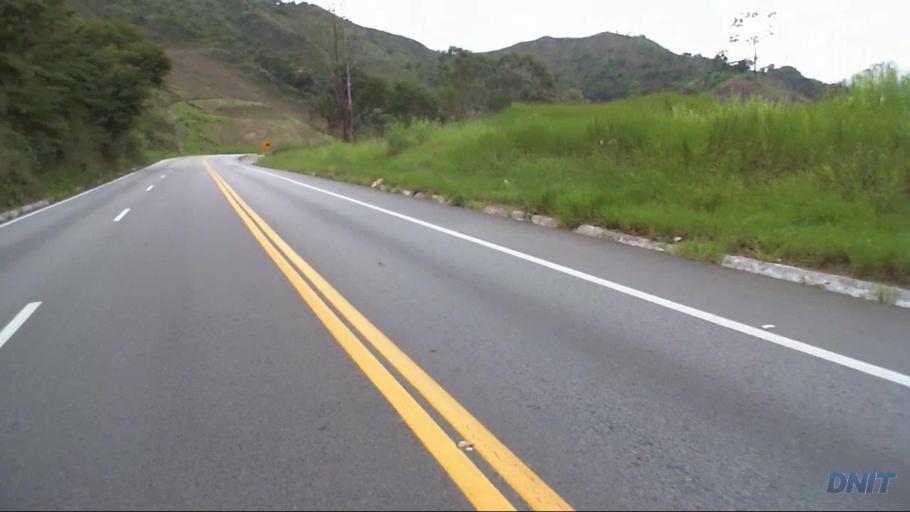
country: BR
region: Minas Gerais
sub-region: Nova Era
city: Nova Era
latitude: -19.6335
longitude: -42.8989
